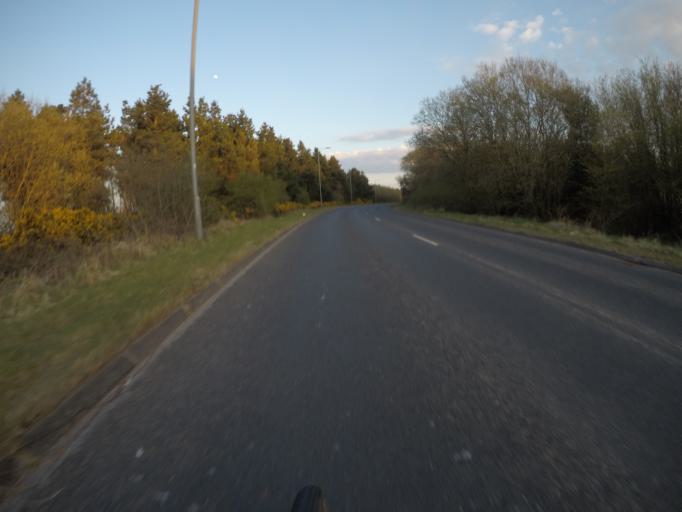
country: GB
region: Scotland
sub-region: North Ayrshire
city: Irvine
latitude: 55.5961
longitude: -4.6694
